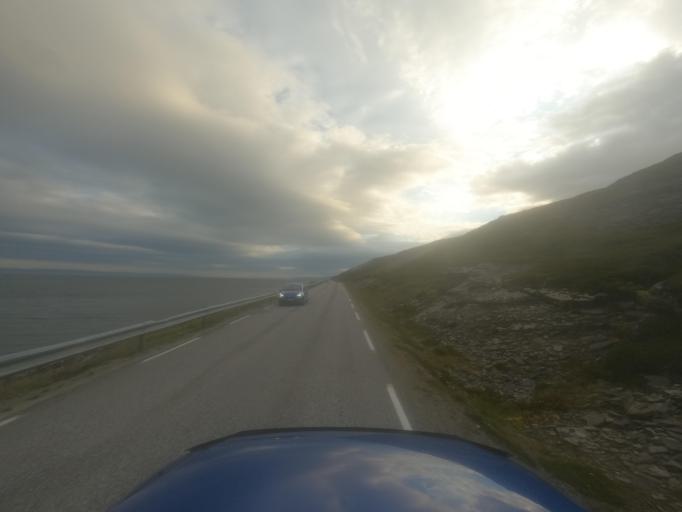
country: NO
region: Finnmark Fylke
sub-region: Nordkapp
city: Honningsvag
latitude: 70.7140
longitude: 25.5689
